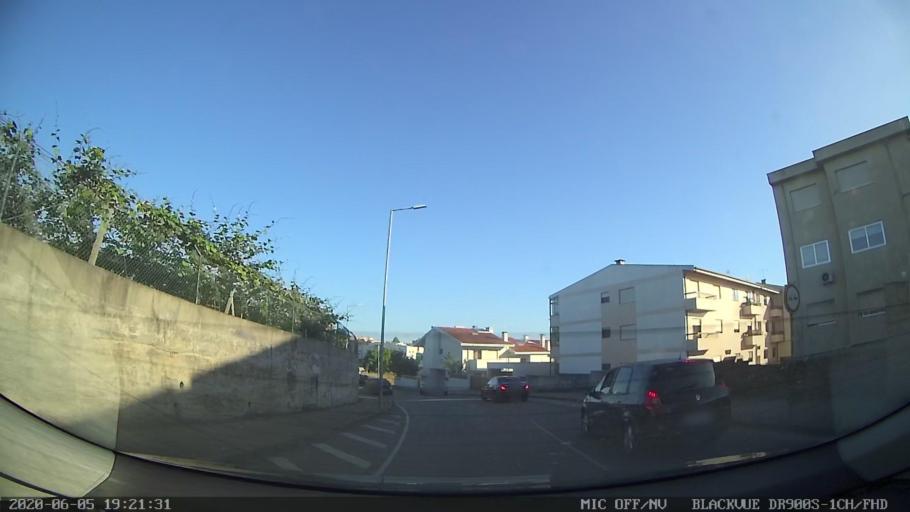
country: PT
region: Porto
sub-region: Gondomar
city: Baguim do Monte
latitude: 41.2080
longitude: -8.5474
